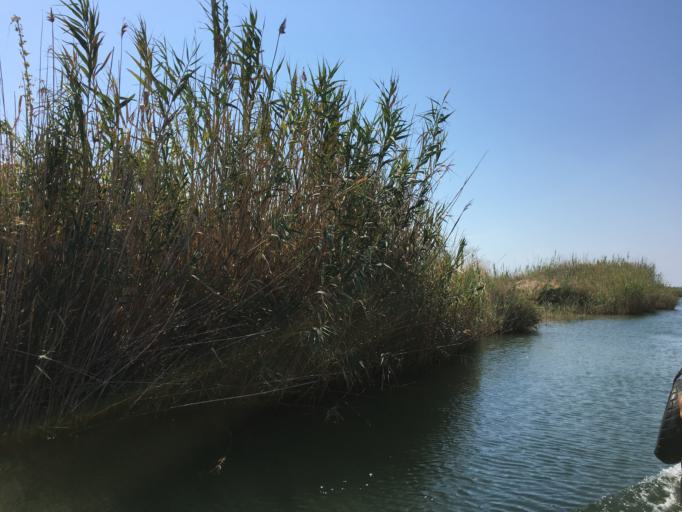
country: TR
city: Dalyan
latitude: 36.8154
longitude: 28.6270
